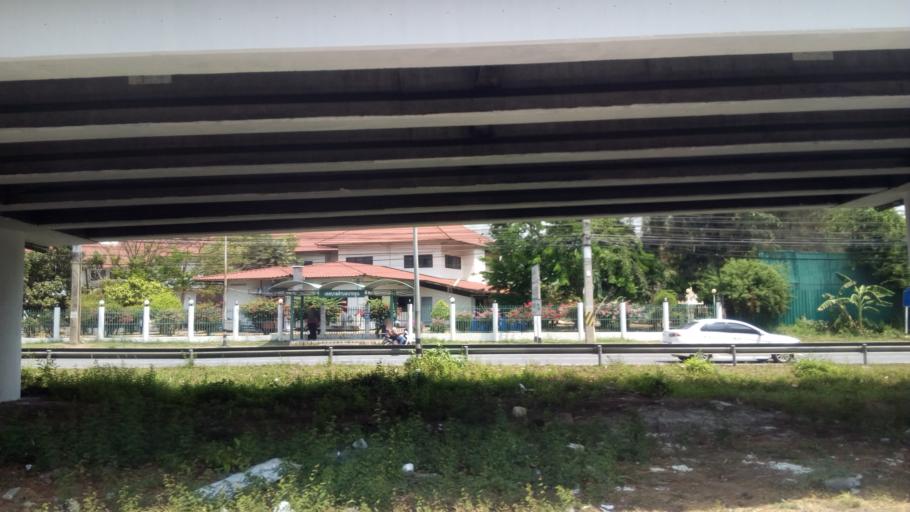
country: TH
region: Phra Nakhon Si Ayutthaya
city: Ban Bang Kadi Pathum Thani
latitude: 13.9842
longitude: 100.5915
